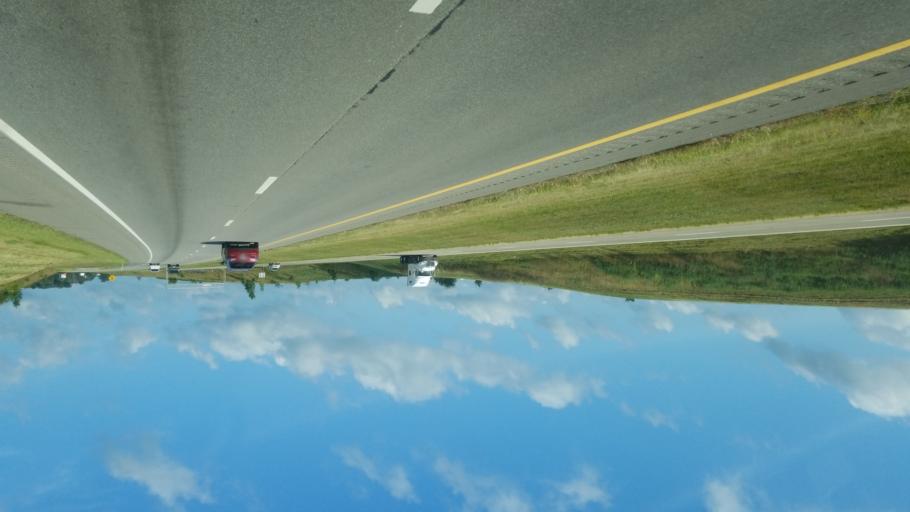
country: US
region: Ohio
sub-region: Wayne County
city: Orrville
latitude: 40.7929
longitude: -81.7867
